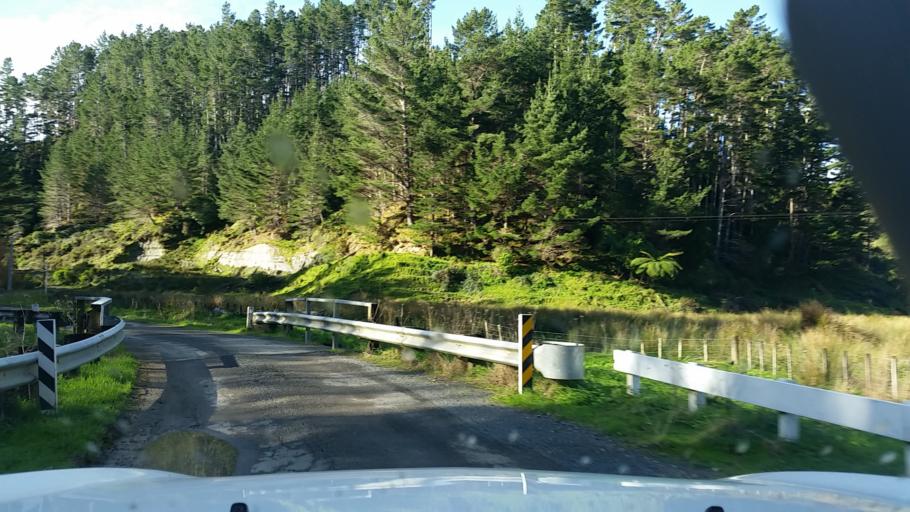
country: NZ
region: Taranaki
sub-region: New Plymouth District
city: Waitara
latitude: -38.9354
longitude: 174.5605
